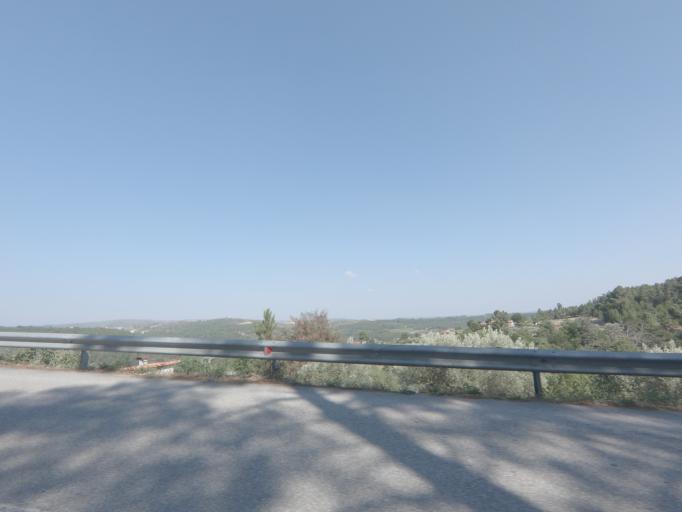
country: PT
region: Viseu
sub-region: Moimenta da Beira
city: Moimenta da Beira
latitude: 40.9800
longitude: -7.5992
